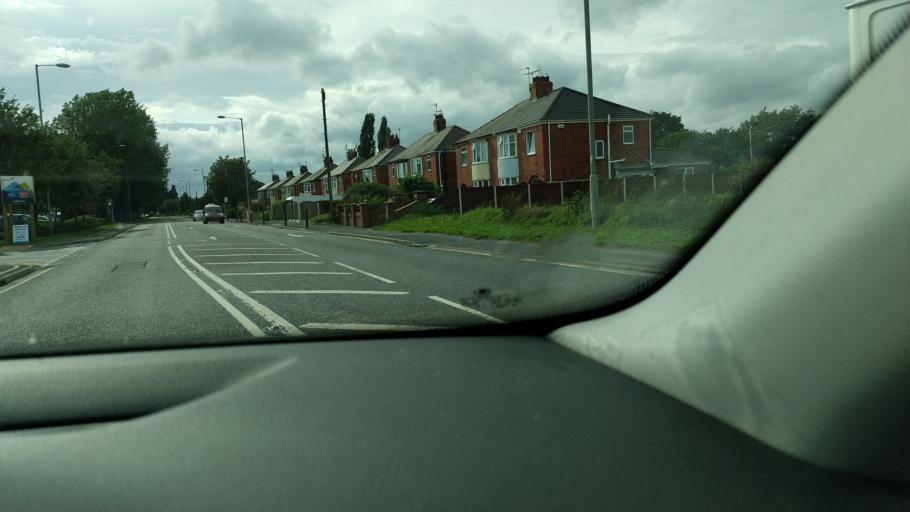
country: GB
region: England
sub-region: East Riding of Yorkshire
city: Airmyn
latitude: 53.7056
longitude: -0.8944
